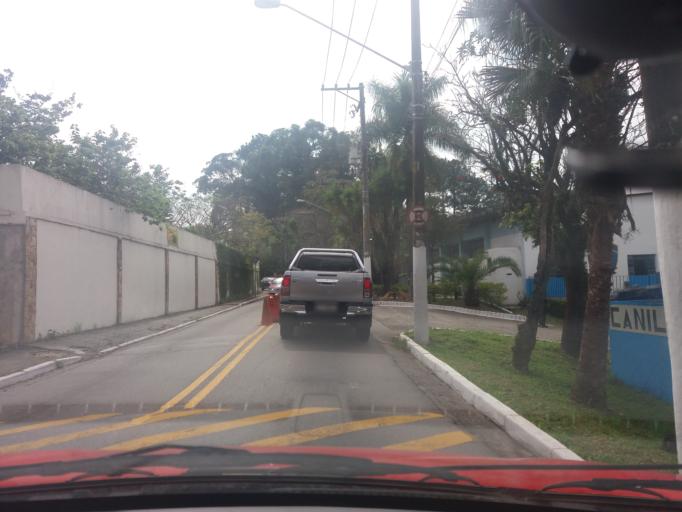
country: BR
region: Sao Paulo
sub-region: Sao Paulo
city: Sao Paulo
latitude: -23.4637
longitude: -46.6272
